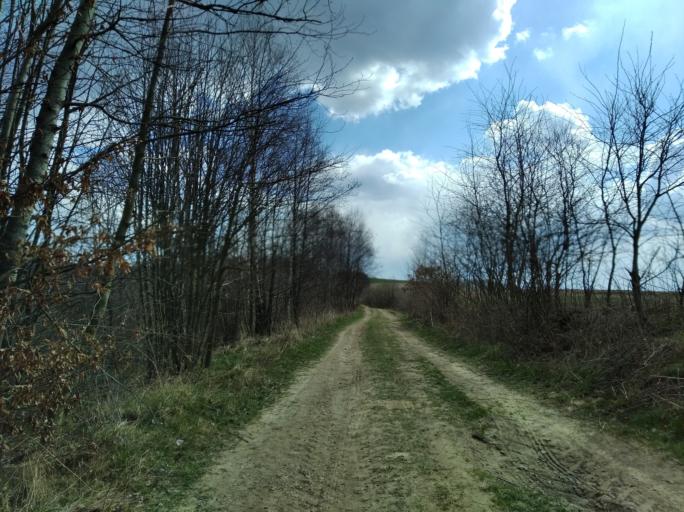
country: PL
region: Subcarpathian Voivodeship
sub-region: Powiat strzyzowski
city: Strzyzow
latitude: 49.9163
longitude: 21.7457
